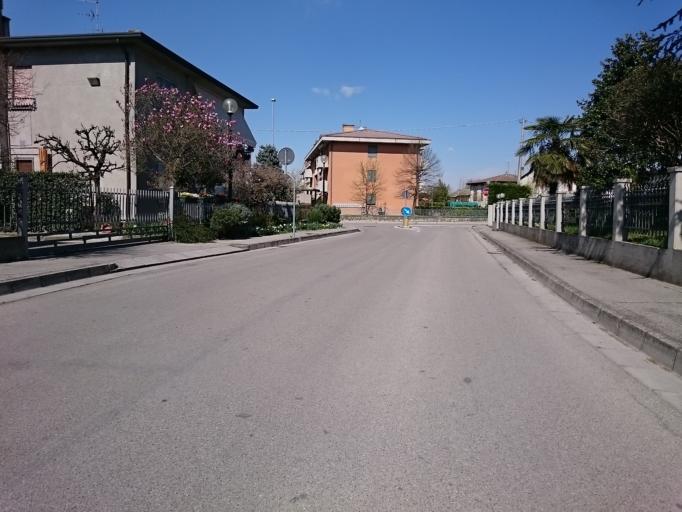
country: IT
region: Veneto
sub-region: Provincia di Padova
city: Brugine
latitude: 45.2986
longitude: 11.9894
